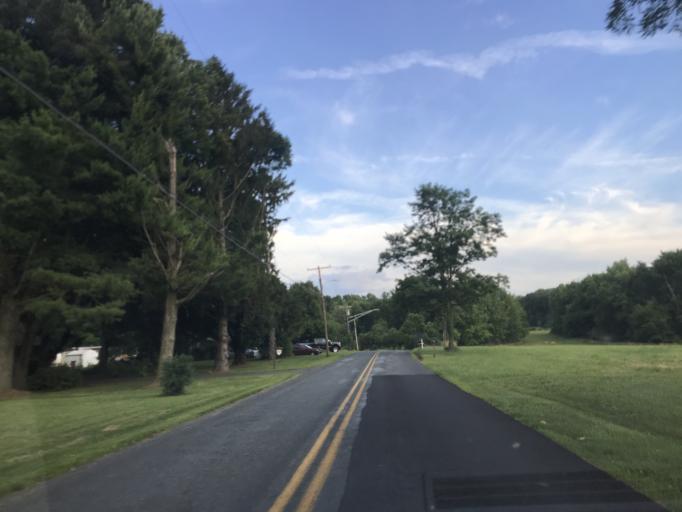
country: US
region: Maryland
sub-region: Harford County
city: Aberdeen
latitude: 39.5286
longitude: -76.2175
